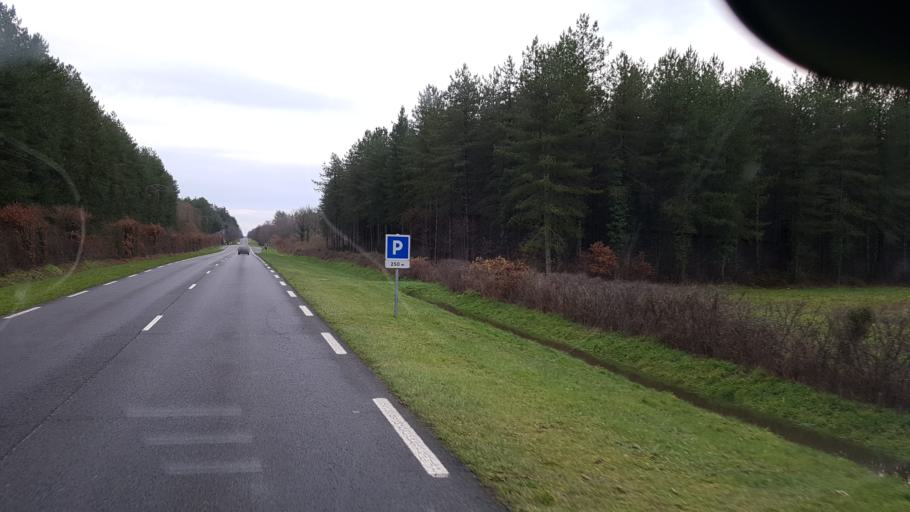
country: FR
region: Centre
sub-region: Departement du Loir-et-Cher
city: Lamotte-Beuvron
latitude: 47.6339
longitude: 2.0023
